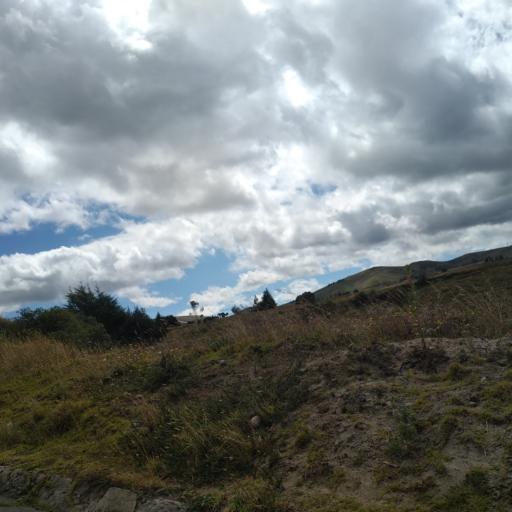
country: EC
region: Cotopaxi
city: Saquisili
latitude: -0.7521
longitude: -78.7301
